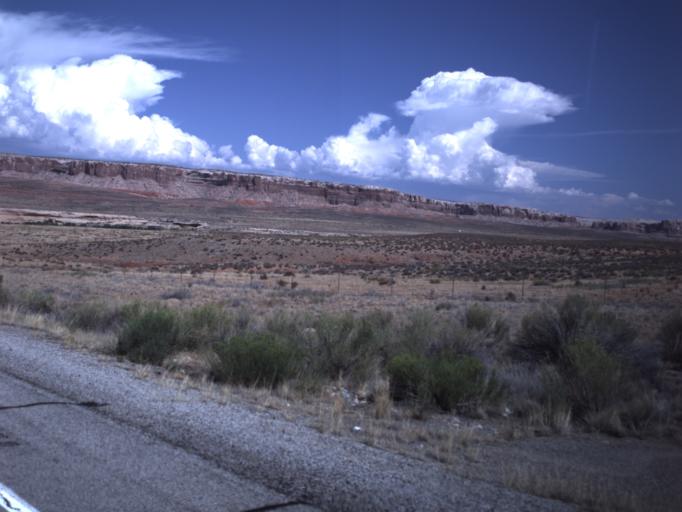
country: US
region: Utah
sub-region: San Juan County
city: Blanding
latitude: 37.2516
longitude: -109.6125
